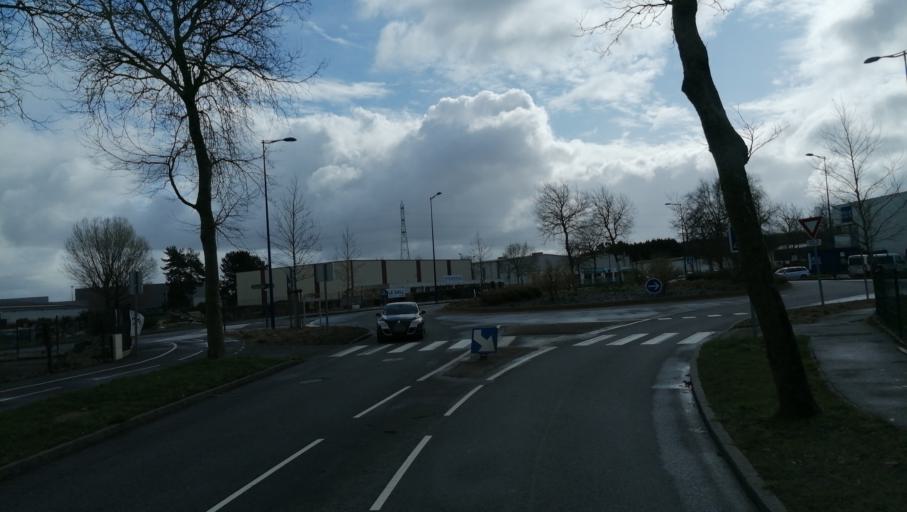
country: FR
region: Brittany
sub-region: Departement des Cotes-d'Armor
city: Ploufragan
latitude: 48.4649
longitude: -2.7867
